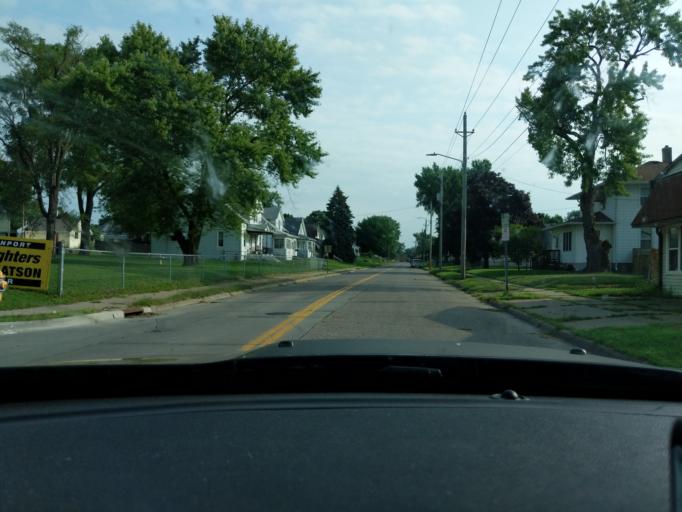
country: US
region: Illinois
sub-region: Rock Island County
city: Rock Island
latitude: 41.5061
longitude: -90.6242
